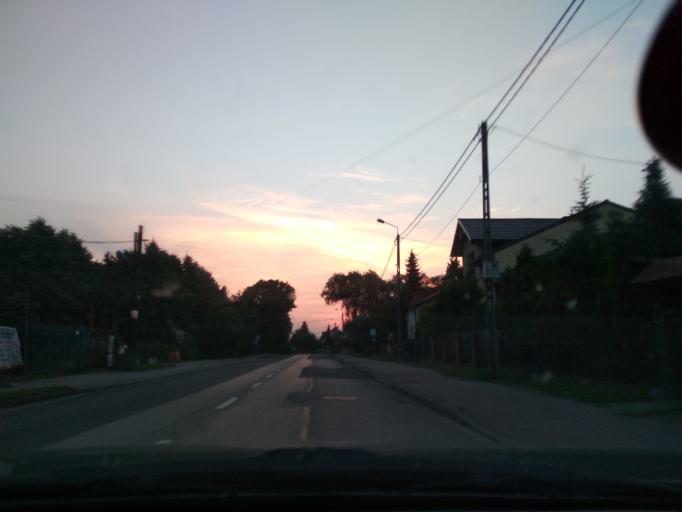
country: PL
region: Silesian Voivodeship
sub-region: Powiat zawiercianski
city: Ogrodzieniec
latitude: 50.4532
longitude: 19.5128
